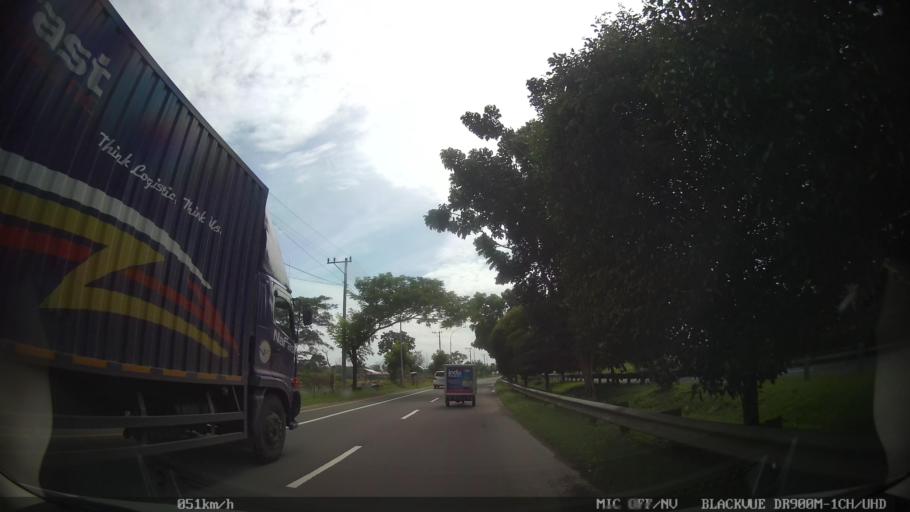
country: ID
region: North Sumatra
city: Percut
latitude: 3.5982
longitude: 98.8113
